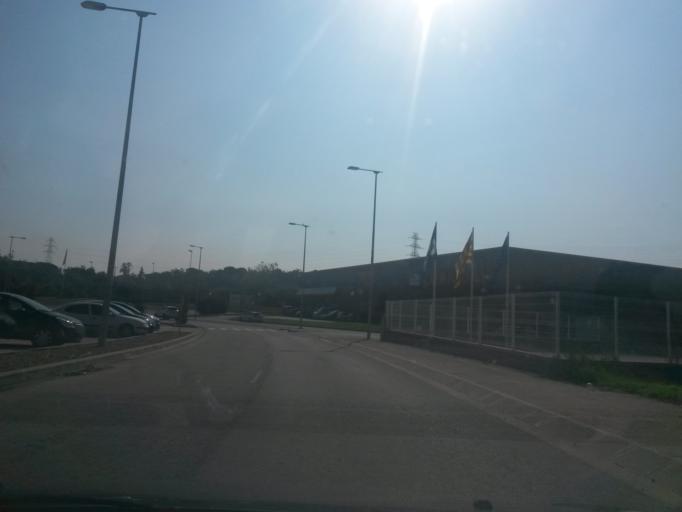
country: ES
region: Catalonia
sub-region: Provincia de Girona
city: Fornells de la Selva
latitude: 41.9413
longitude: 2.8014
